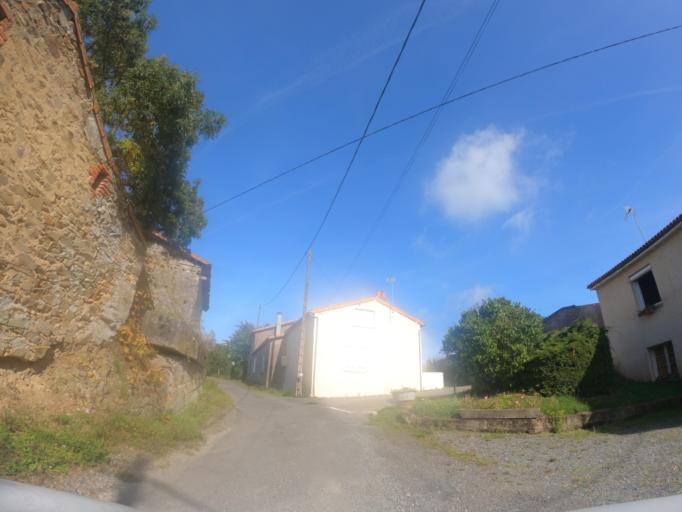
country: FR
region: Poitou-Charentes
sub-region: Departement des Deux-Sevres
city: Courlay
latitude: 46.7932
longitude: -0.5859
